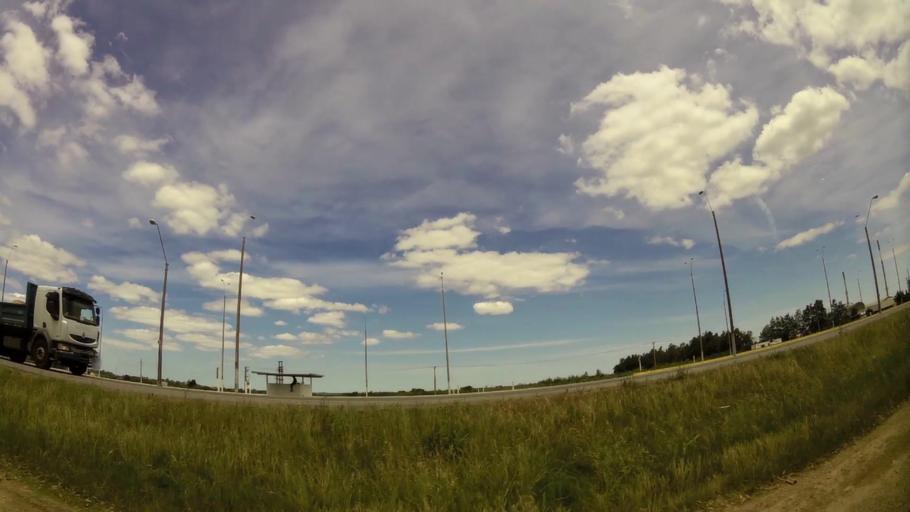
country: UY
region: San Jose
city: Delta del Tigre
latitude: -34.7757
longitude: -56.3681
